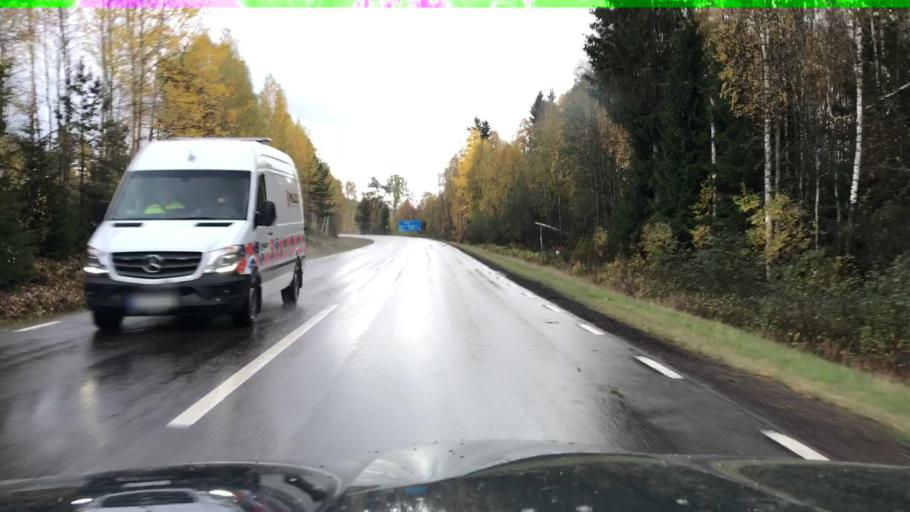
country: SE
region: Vaermland
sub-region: Hagfors Kommun
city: Ekshaerad
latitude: 60.4269
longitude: 13.2501
